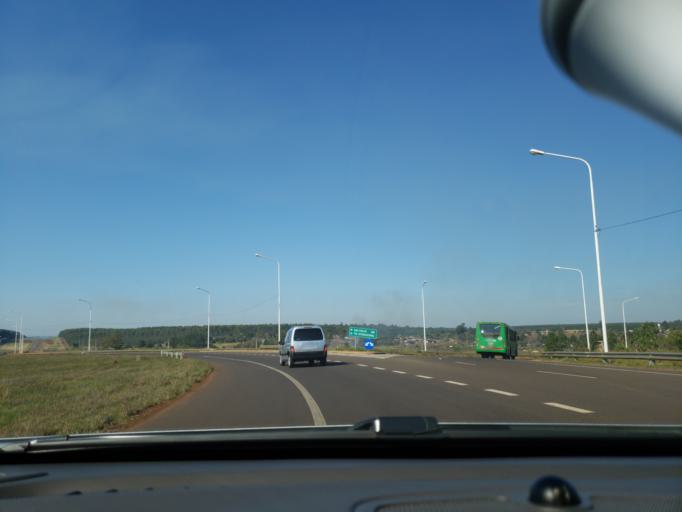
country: AR
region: Misiones
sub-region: Departamento de Capital
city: Posadas
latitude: -27.4654
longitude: -55.9714
